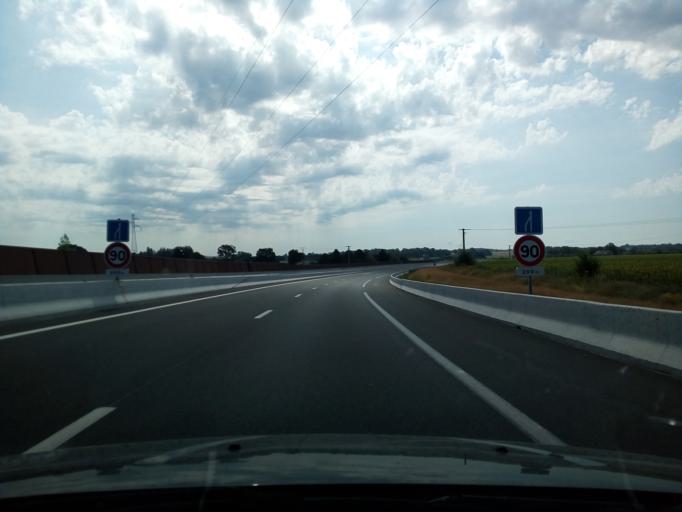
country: FR
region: Auvergne
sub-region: Departement de l'Allier
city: Varennes-sur-Allier
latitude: 46.3052
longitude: 3.4133
